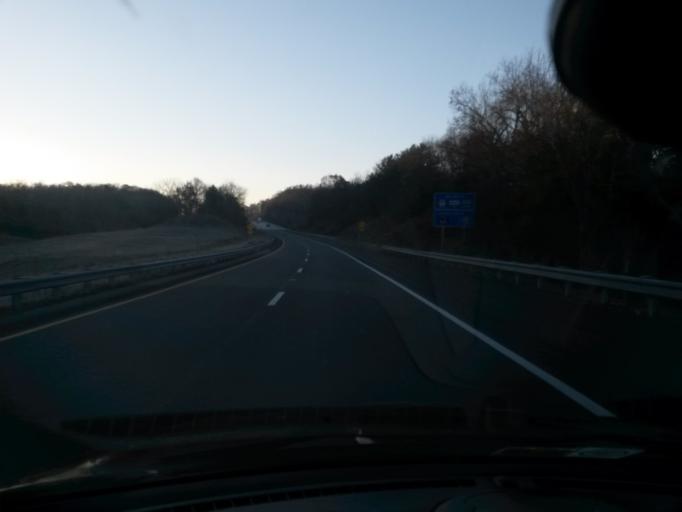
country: US
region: Virginia
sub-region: Rockbridge County
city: East Lexington
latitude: 37.8178
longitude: -79.4423
